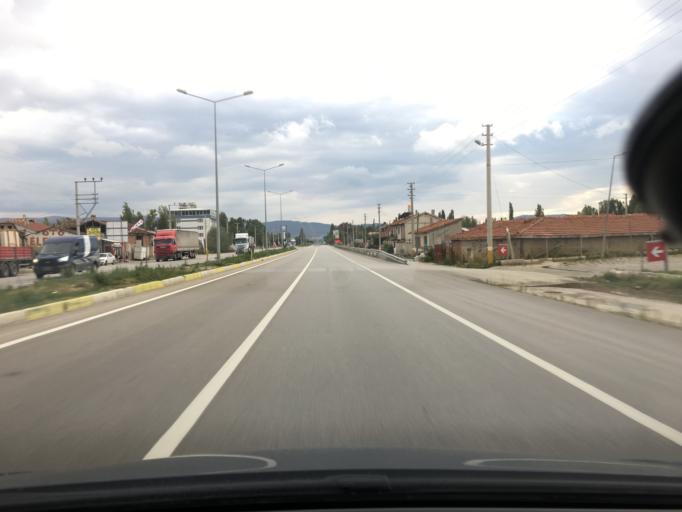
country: TR
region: Afyonkarahisar
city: Sincanli
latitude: 38.7717
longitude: 30.3693
